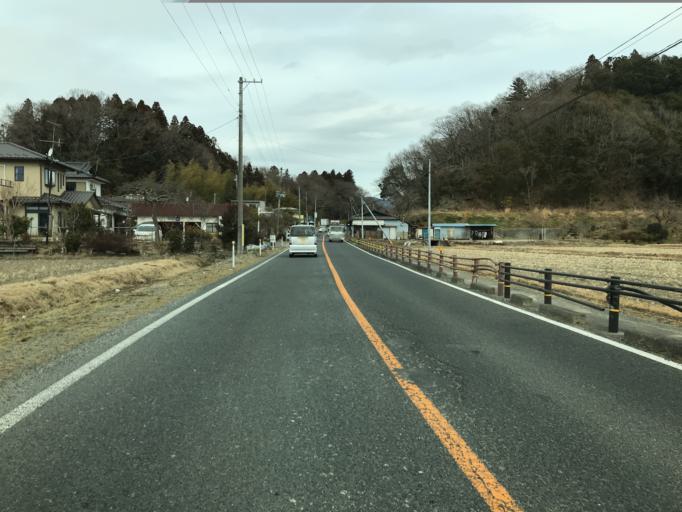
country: JP
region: Fukushima
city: Iwaki
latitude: 37.0916
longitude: 140.8730
